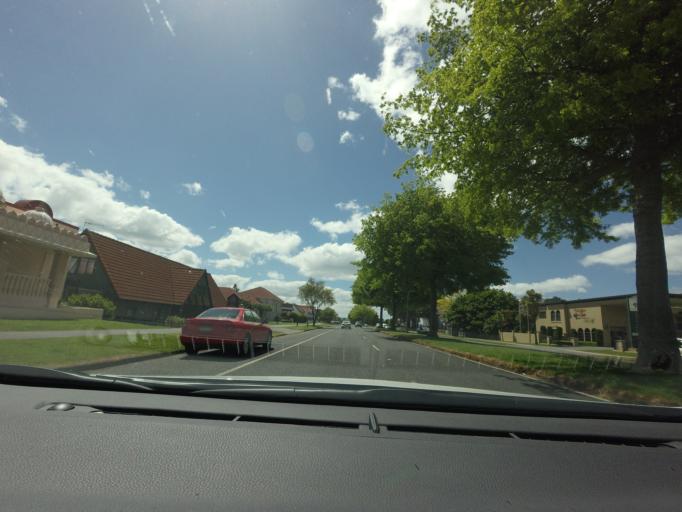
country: NZ
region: Bay of Plenty
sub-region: Rotorua District
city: Rotorua
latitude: -38.1498
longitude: 176.2537
